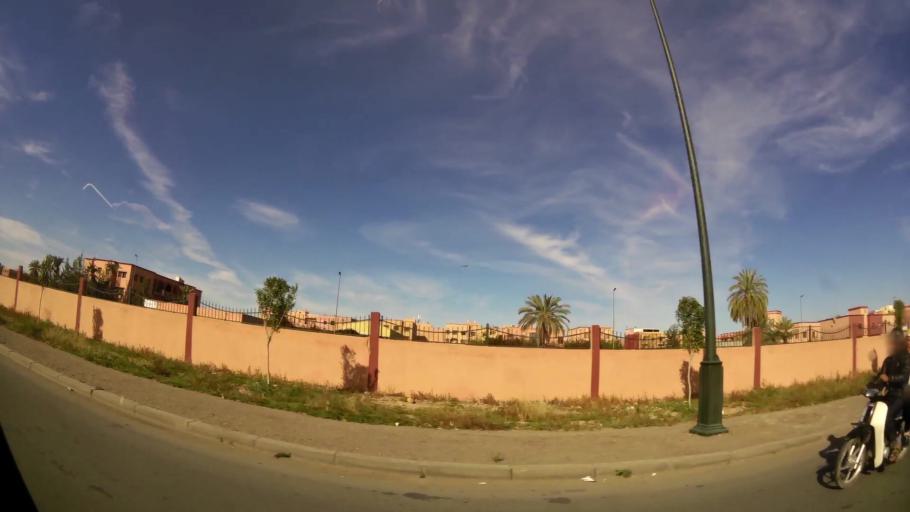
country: MA
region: Marrakech-Tensift-Al Haouz
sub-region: Marrakech
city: Marrakesh
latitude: 31.6725
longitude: -8.0419
